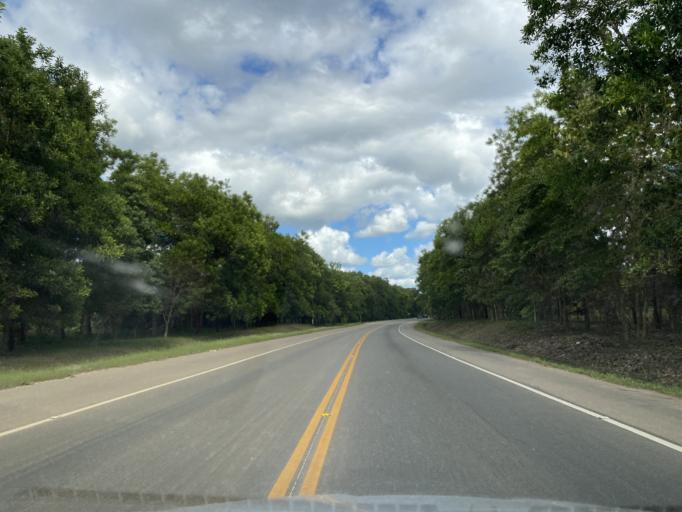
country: DO
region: Santo Domingo
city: Guerra
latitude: 18.6560
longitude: -69.7489
